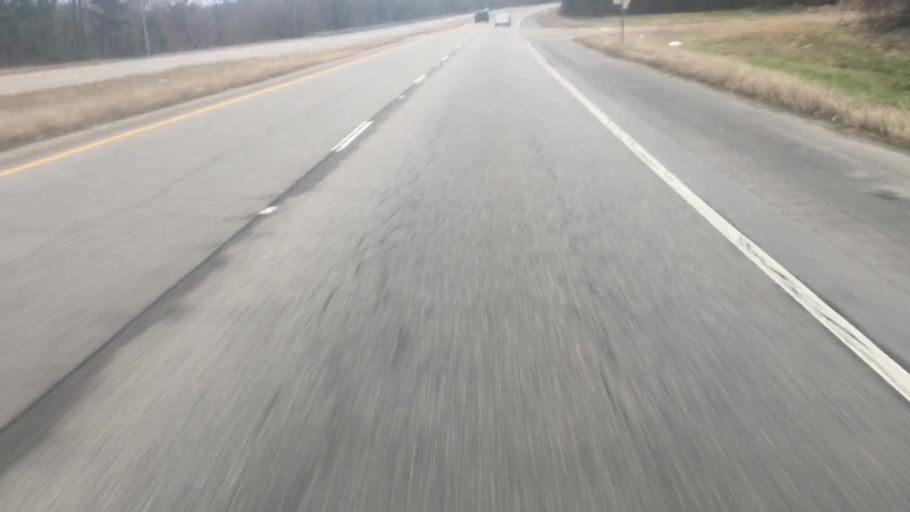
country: US
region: Alabama
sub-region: Walker County
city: Cordova
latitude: 33.8178
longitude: -87.1510
